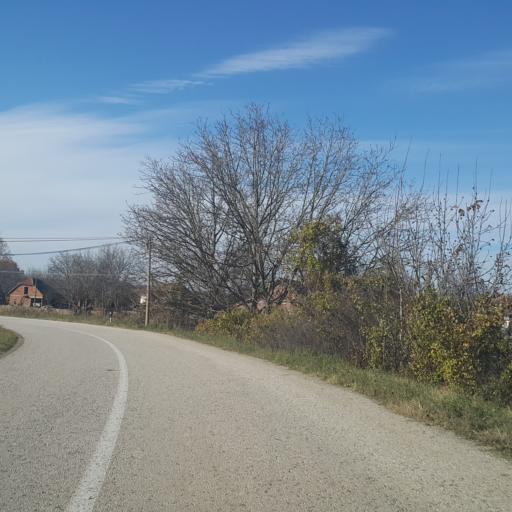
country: RS
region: Central Serbia
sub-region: Sumadijski Okrug
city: Topola
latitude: 44.2584
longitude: 20.8245
